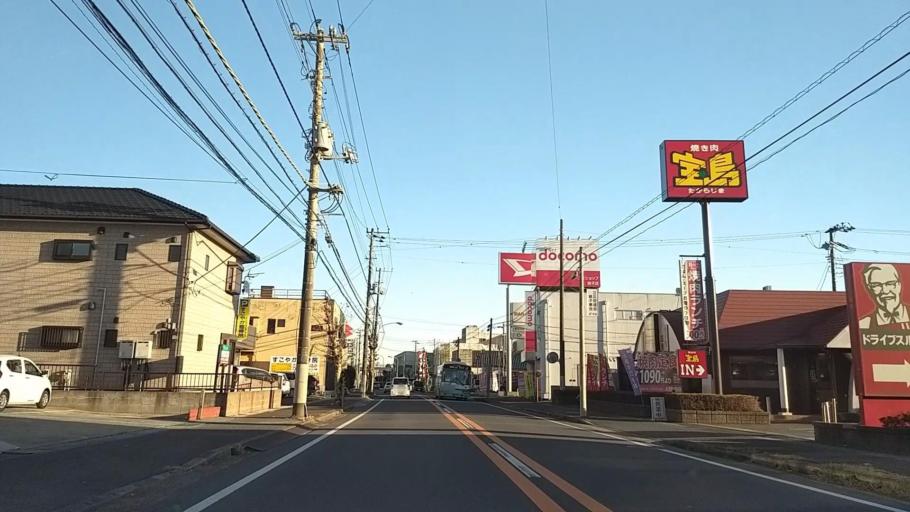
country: JP
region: Chiba
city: Hasaki
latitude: 35.7399
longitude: 140.7983
